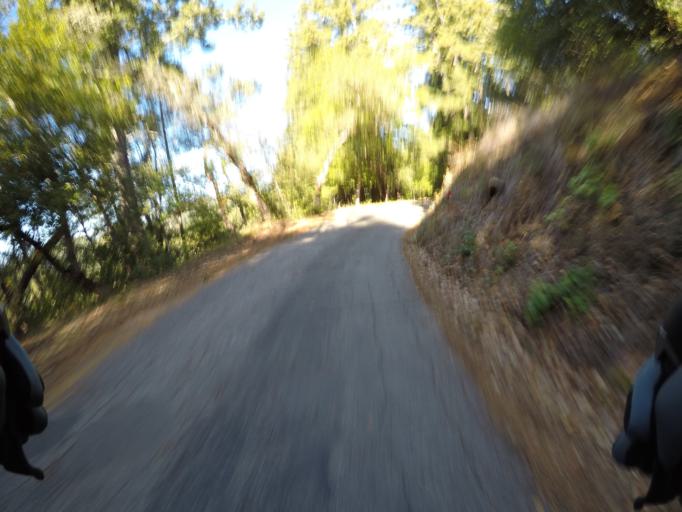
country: US
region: California
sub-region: Santa Clara County
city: Lexington Hills
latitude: 37.1080
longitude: -121.9925
